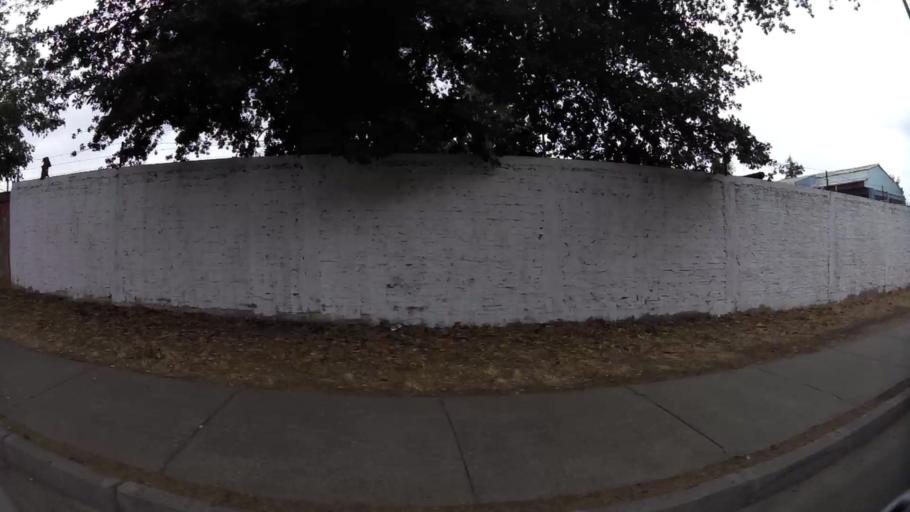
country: CL
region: O'Higgins
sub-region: Provincia de Cachapoal
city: Graneros
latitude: -34.0711
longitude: -70.7234
